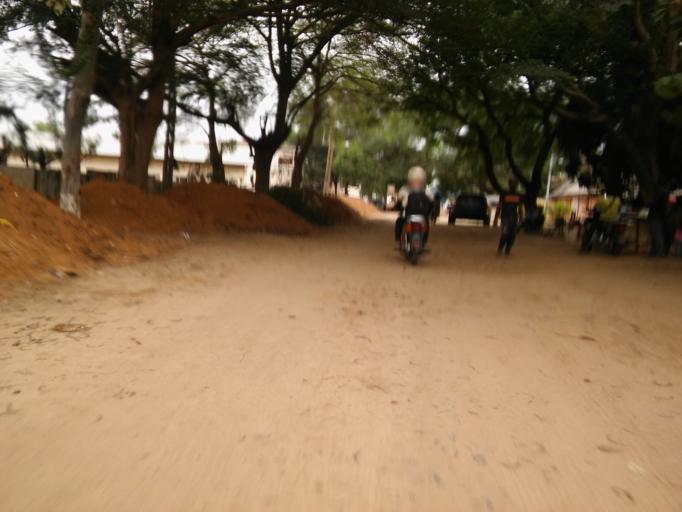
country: BJ
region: Littoral
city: Cotonou
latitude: 6.3550
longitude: 2.3930
